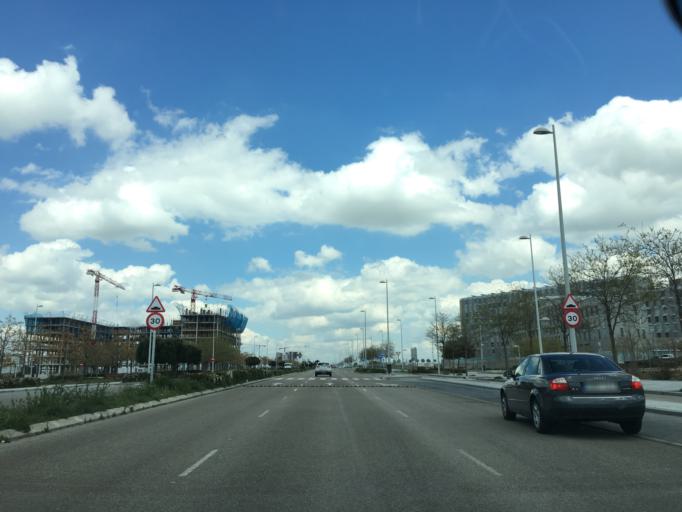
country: ES
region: Madrid
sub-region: Provincia de Madrid
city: Hortaleza
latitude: 40.4856
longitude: -3.6148
